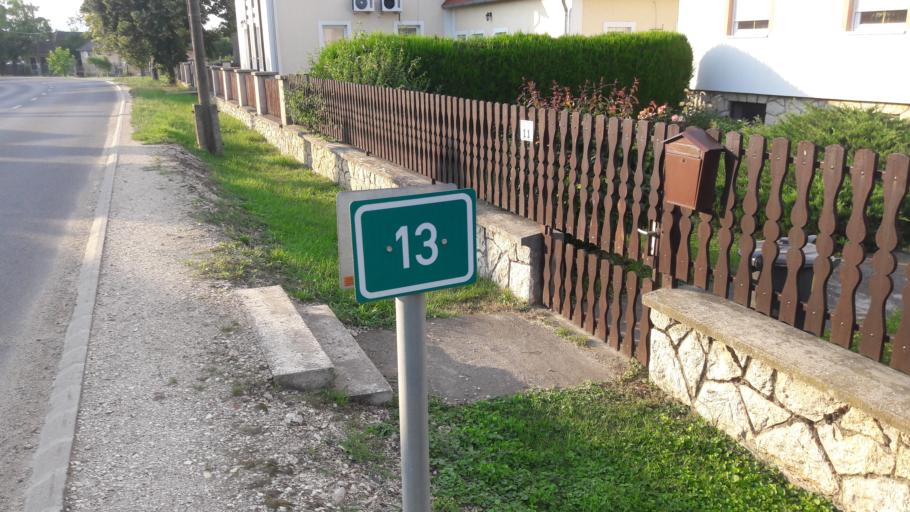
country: HU
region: Veszprem
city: Zanka
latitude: 46.9792
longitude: 17.7032
